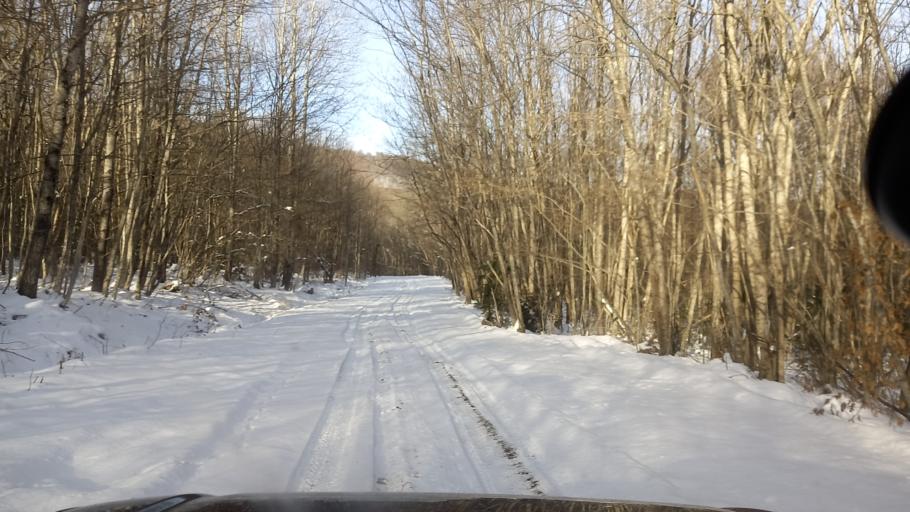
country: RU
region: Adygeya
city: Kamennomostskiy
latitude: 44.2248
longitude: 40.0993
